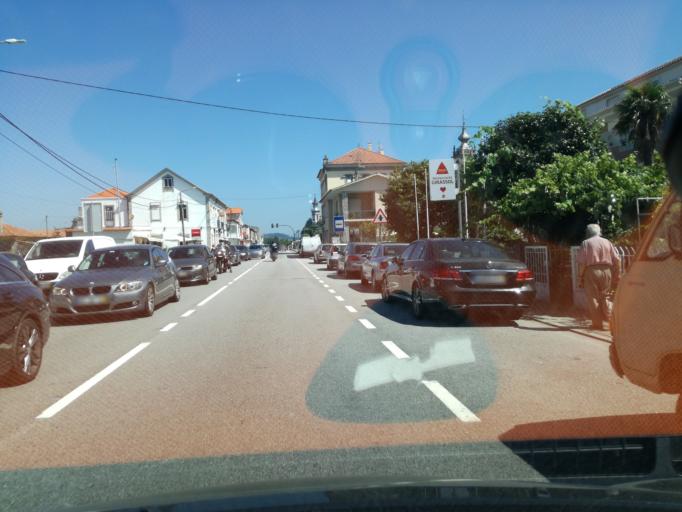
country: ES
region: Galicia
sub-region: Provincia de Pontevedra
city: O Rosal
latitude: 41.8953
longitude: -8.8194
